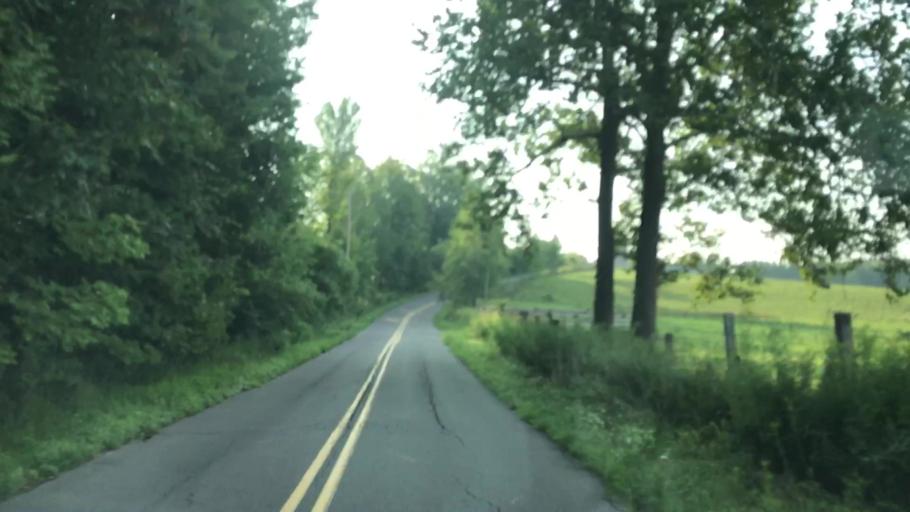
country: US
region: Pennsylvania
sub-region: Wyoming County
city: Factoryville
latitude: 41.6097
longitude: -75.7353
